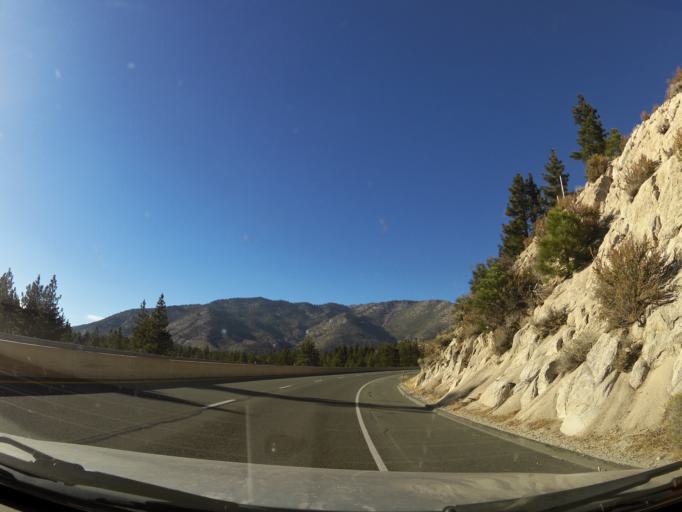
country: US
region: Nevada
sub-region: Douglas County
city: Indian Hills
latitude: 39.1157
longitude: -119.8115
